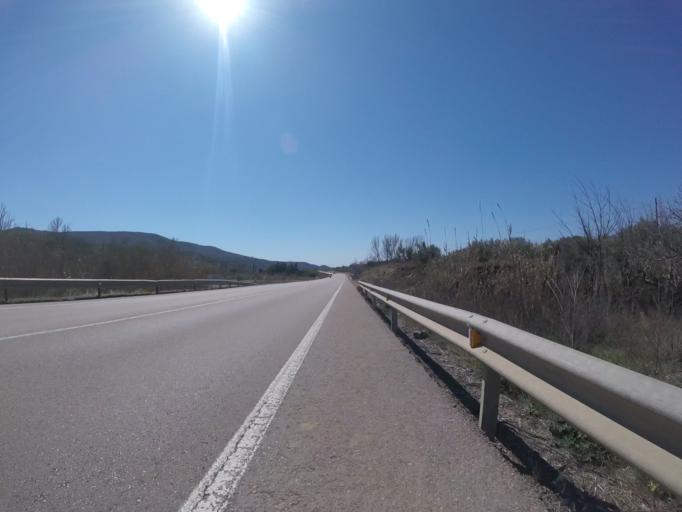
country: ES
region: Valencia
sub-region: Provincia de Castello
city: Cuevas de Vinroma
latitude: 40.3821
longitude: 0.1454
